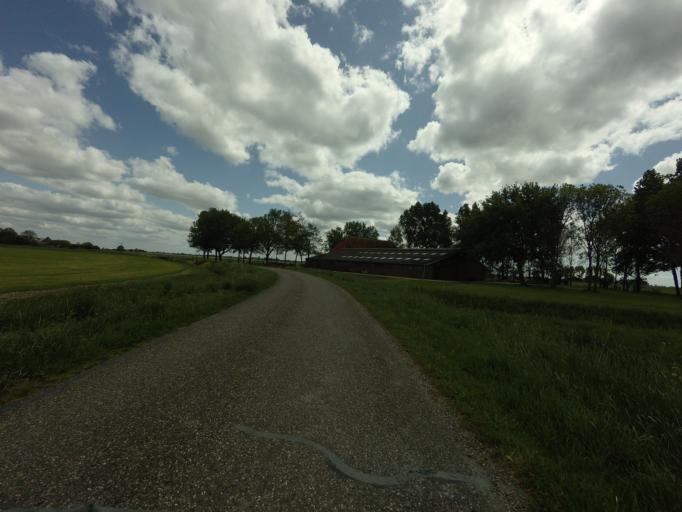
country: NL
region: Friesland
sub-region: Gemeente Franekeradeel
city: Tzum
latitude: 53.1370
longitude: 5.5578
